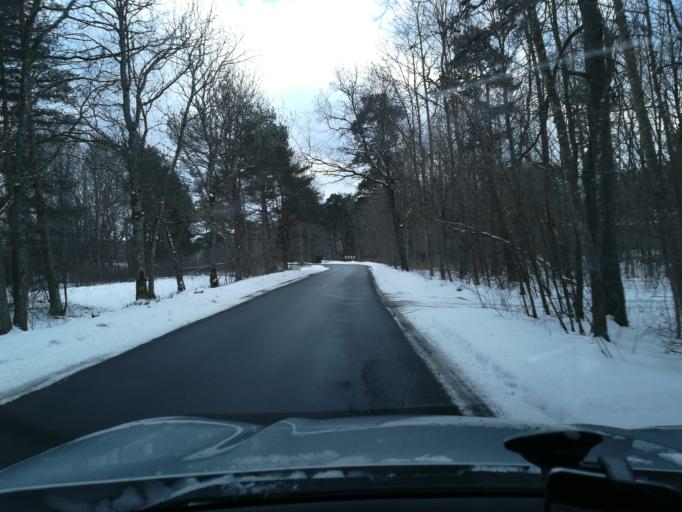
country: EE
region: Harju
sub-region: Paldiski linn
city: Paldiski
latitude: 59.3780
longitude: 24.2357
